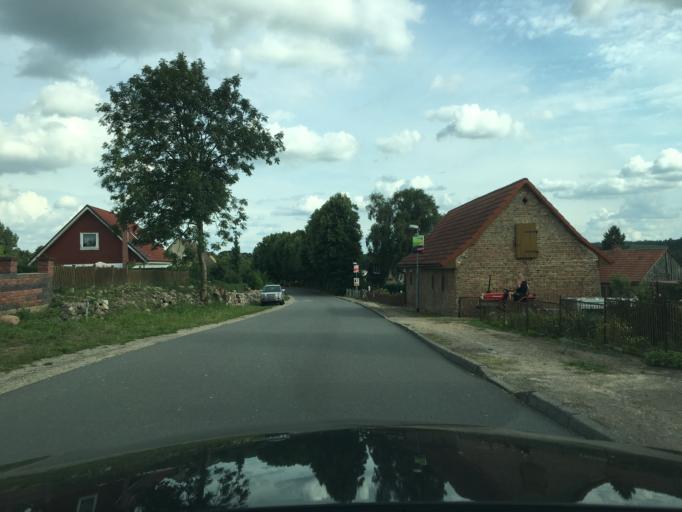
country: DE
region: Mecklenburg-Vorpommern
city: Mollenhagen
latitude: 53.4822
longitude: 12.9618
